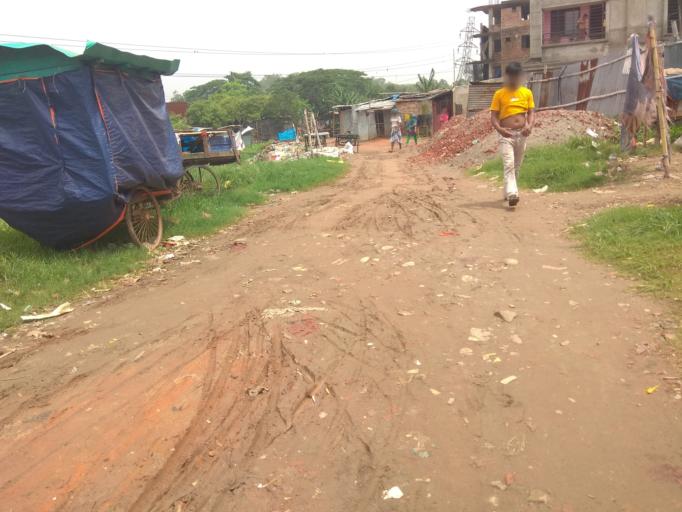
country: BD
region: Dhaka
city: Tungi
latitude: 23.8158
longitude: 90.3527
